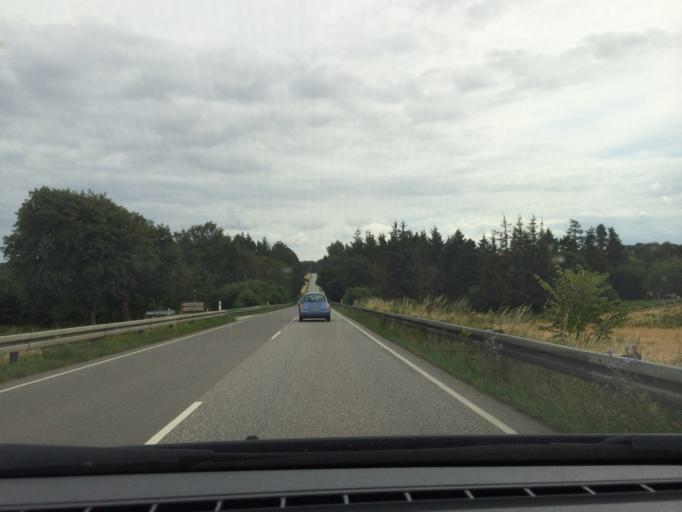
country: DK
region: Zealand
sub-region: Vordingborg Kommune
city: Praesto
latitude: 55.1025
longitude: 12.0722
